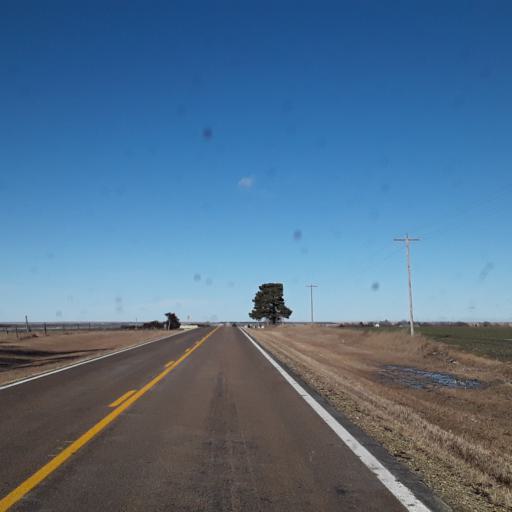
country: US
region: Kansas
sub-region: Mitchell County
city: Beloit
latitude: 39.3461
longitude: -98.1161
